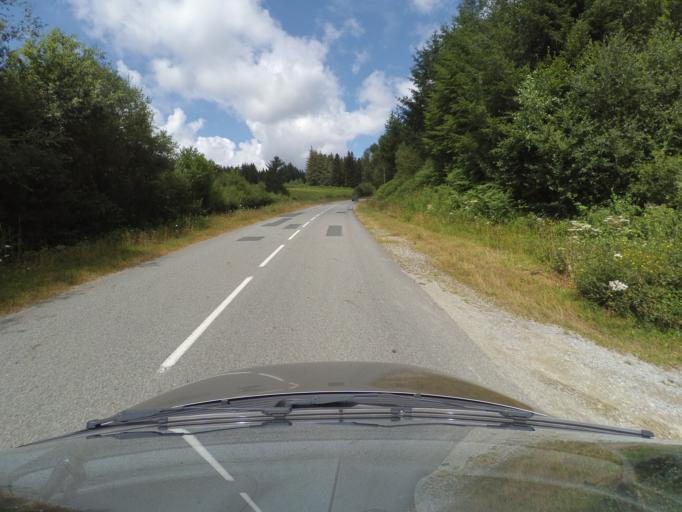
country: FR
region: Limousin
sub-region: Departement de la Creuse
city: Bourganeuf
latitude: 45.9213
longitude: 1.8449
